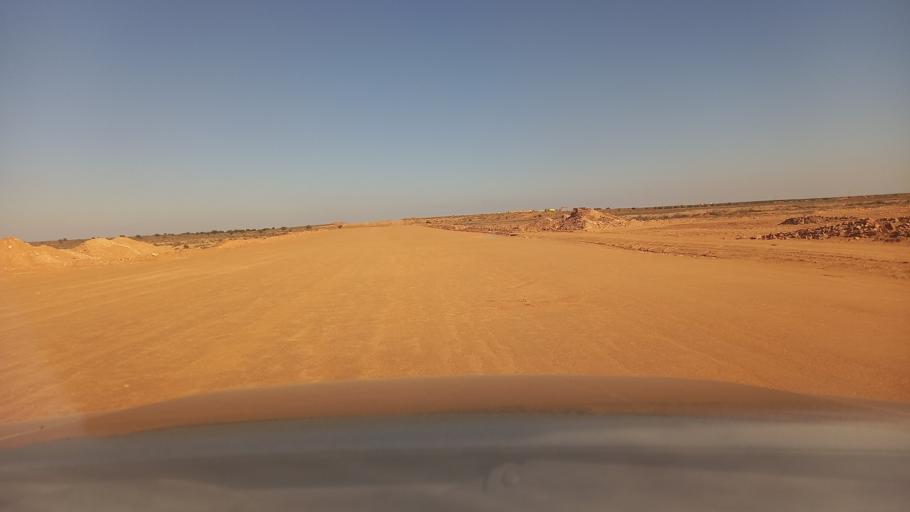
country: TN
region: Madanin
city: Medenine
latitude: 33.1702
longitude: 10.5259
